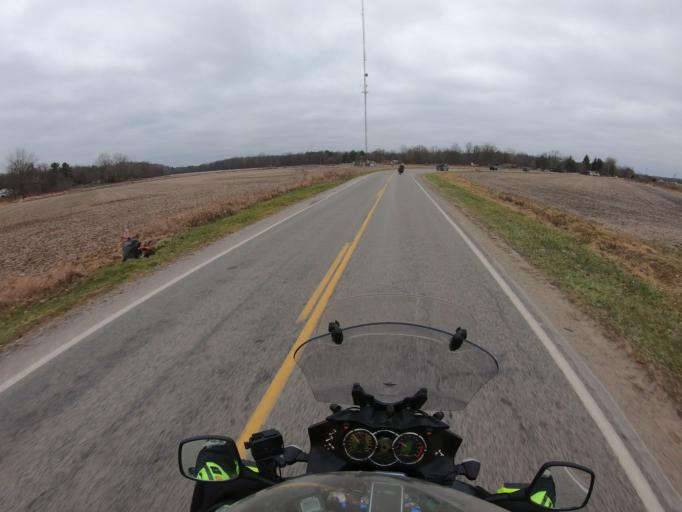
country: US
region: Michigan
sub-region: Saginaw County
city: Saint Charles
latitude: 43.2819
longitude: -84.1351
